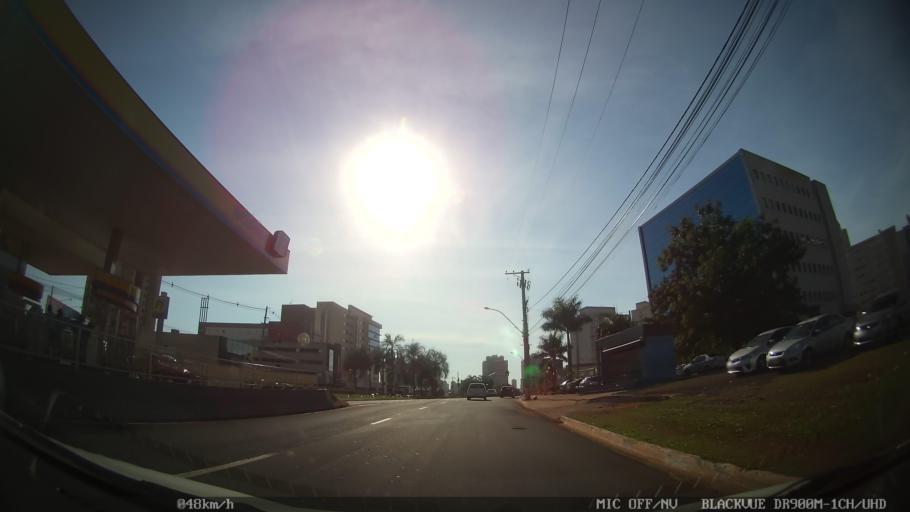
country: BR
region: Sao Paulo
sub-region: Ribeirao Preto
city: Ribeirao Preto
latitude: -21.2175
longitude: -47.8255
